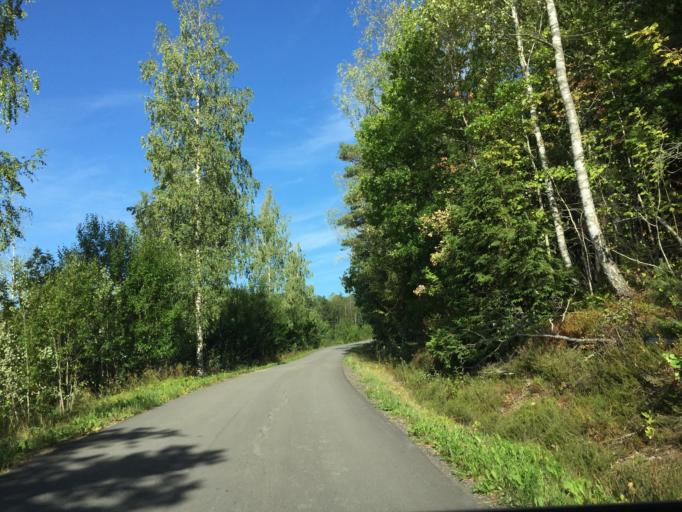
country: NO
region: Vestfold
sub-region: Holmestrand
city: Gullhaug
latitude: 59.4837
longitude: 10.1721
